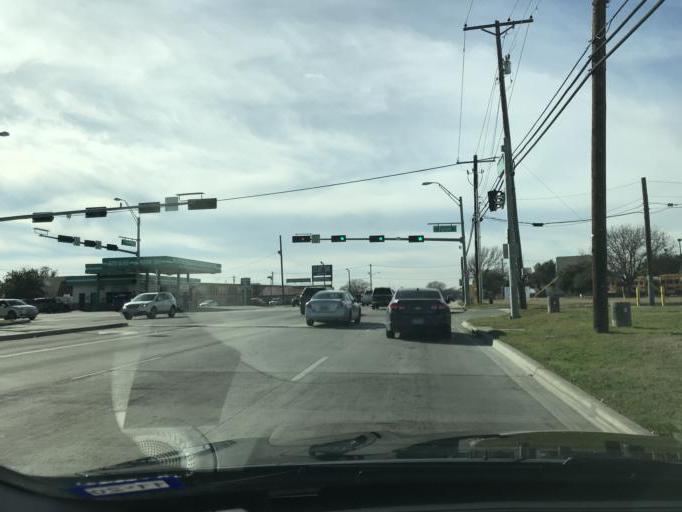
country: US
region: Texas
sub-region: Denton County
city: Denton
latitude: 33.2298
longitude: -97.1427
